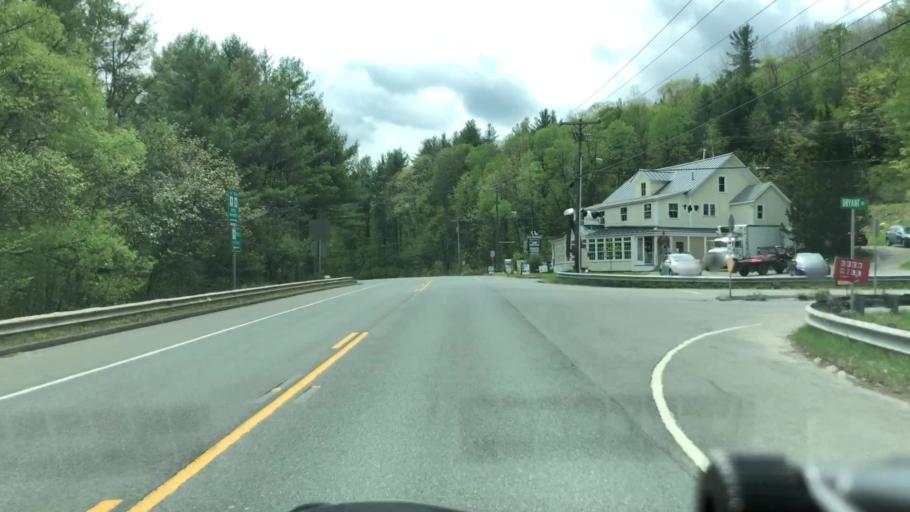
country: US
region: Massachusetts
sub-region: Hampshire County
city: Chesterfield
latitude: 42.4647
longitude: -72.9053
